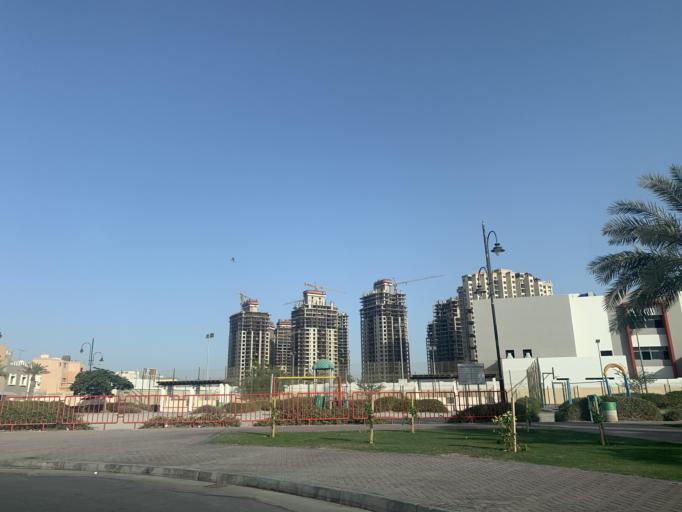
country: BH
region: Manama
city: Jidd Hafs
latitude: 26.2070
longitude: 50.4476
